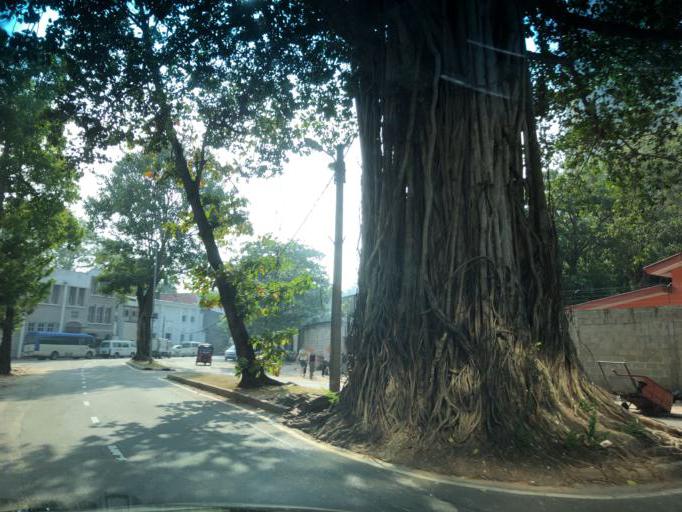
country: LK
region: Western
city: Colombo
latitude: 6.9173
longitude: 79.8576
